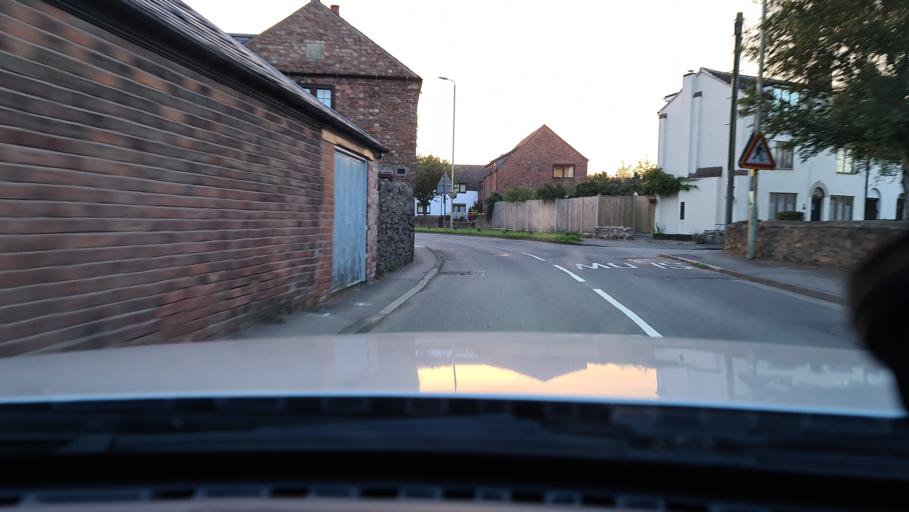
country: GB
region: England
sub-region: Leicestershire
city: Sapcote
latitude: 52.5363
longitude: -1.2802
